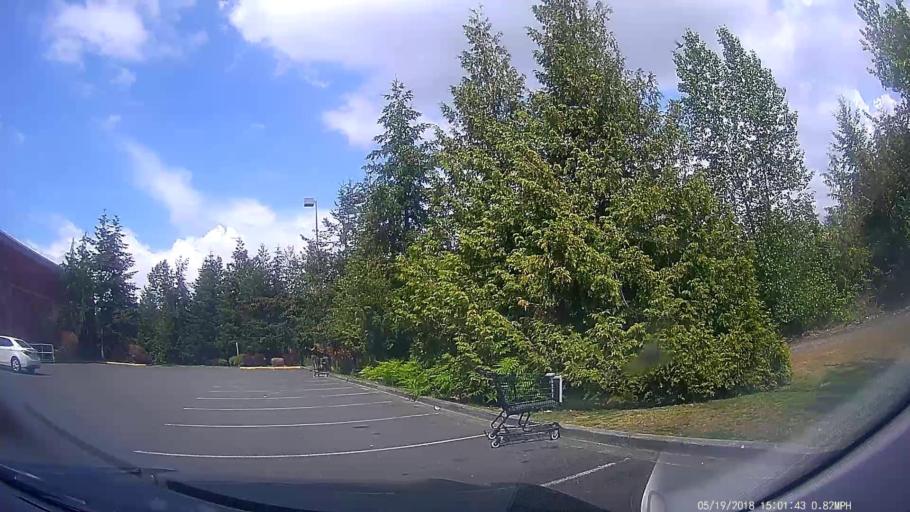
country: US
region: Washington
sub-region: Skagit County
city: Mount Vernon
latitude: 48.4220
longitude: -122.3069
